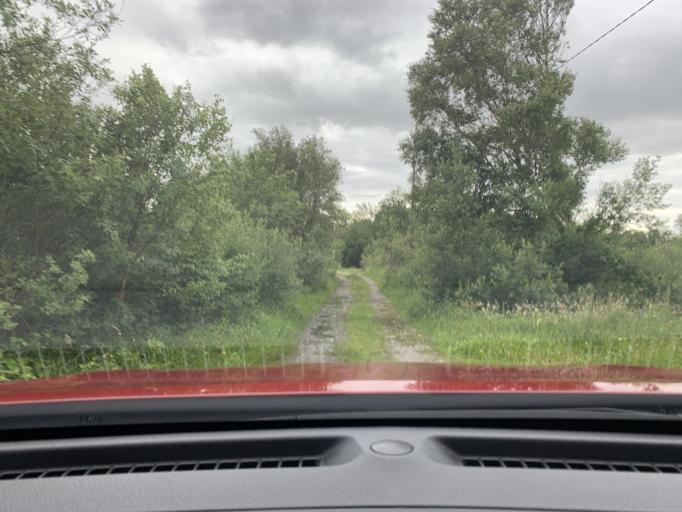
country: IE
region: Connaught
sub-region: County Leitrim
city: Kinlough
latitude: 54.4558
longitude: -8.3589
